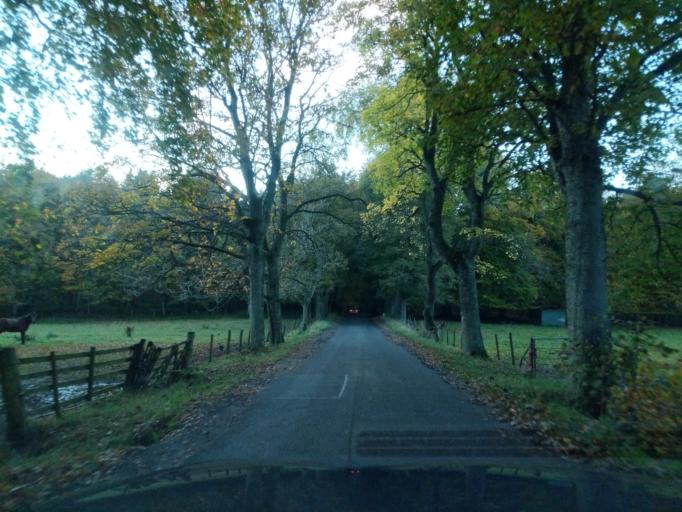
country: GB
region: Scotland
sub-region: Fife
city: Leuchars
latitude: 56.4038
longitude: -2.8351
